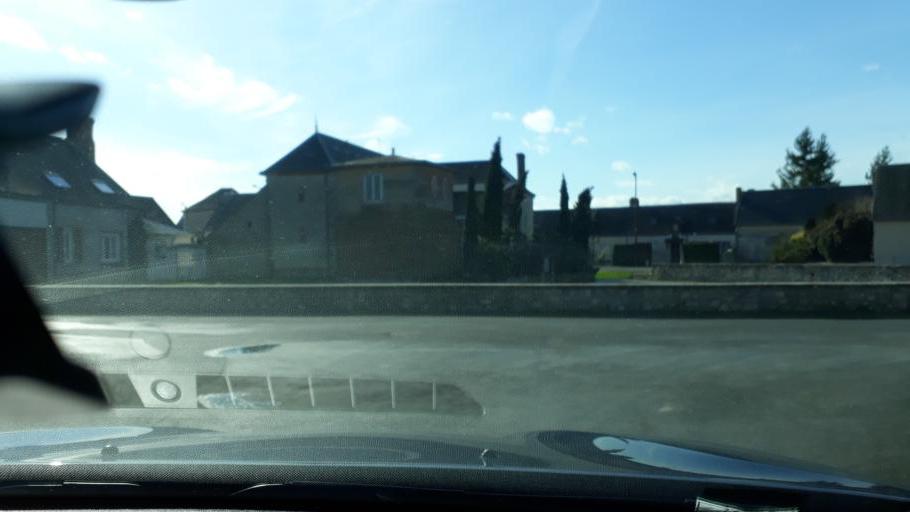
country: FR
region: Centre
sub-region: Departement du Loiret
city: Ascheres-le-Marche
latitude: 48.0852
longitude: 1.9540
